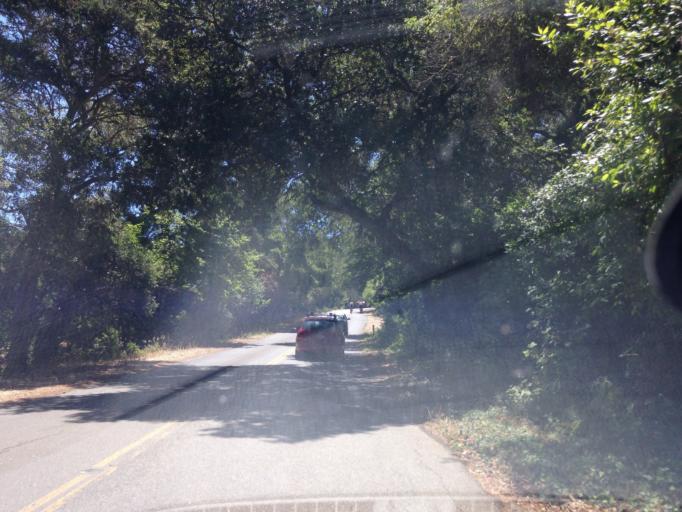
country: US
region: California
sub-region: Contra Costa County
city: Kensington
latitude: 37.9054
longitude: -122.2627
